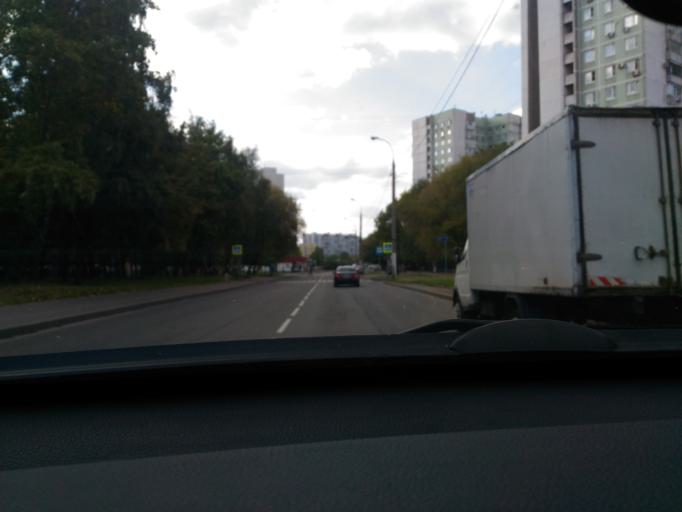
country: RU
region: Moscow
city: Vatutino
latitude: 55.8839
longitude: 37.6895
